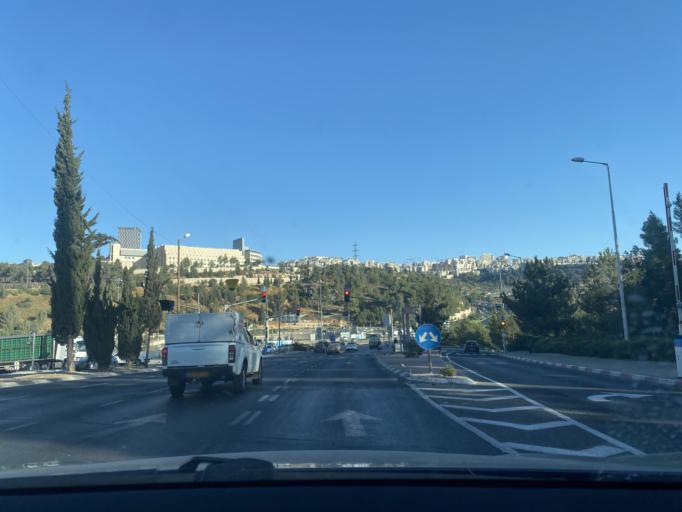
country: PS
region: West Bank
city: Bayt Iksa
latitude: 31.8095
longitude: 35.2038
